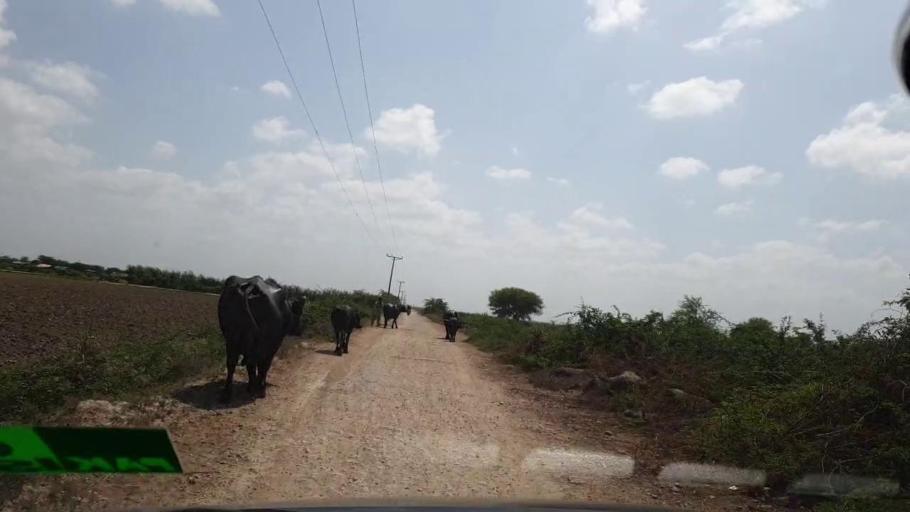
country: PK
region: Sindh
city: Kadhan
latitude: 24.6114
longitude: 69.1853
